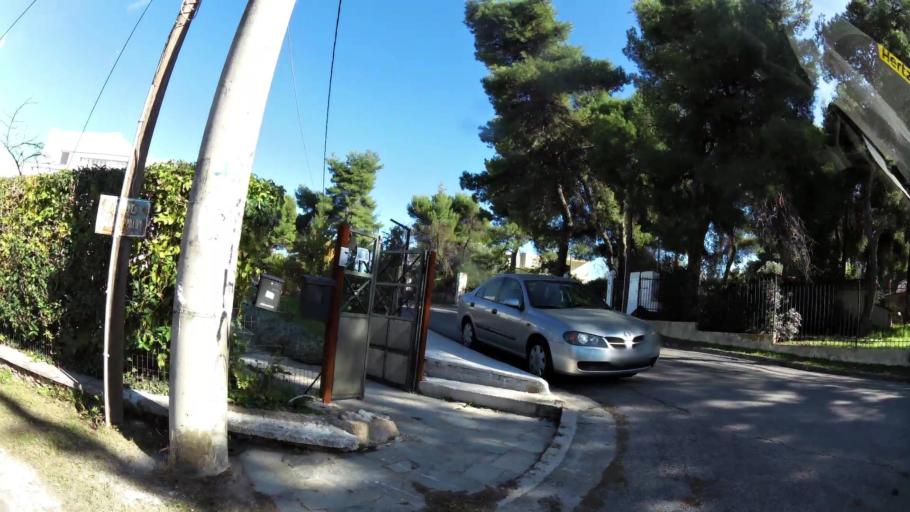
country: GR
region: Attica
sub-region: Nomarchia Anatolikis Attikis
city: Drosia
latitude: 38.1169
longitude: 23.8697
